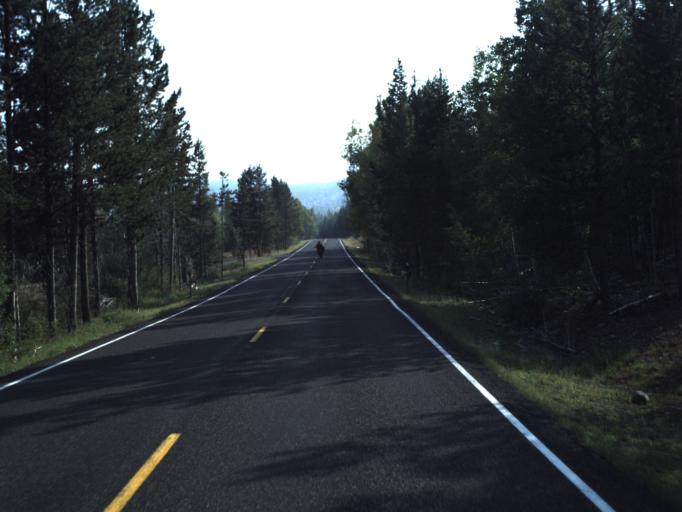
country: US
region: Utah
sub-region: Summit County
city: Oakley
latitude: 40.8030
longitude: -110.8802
